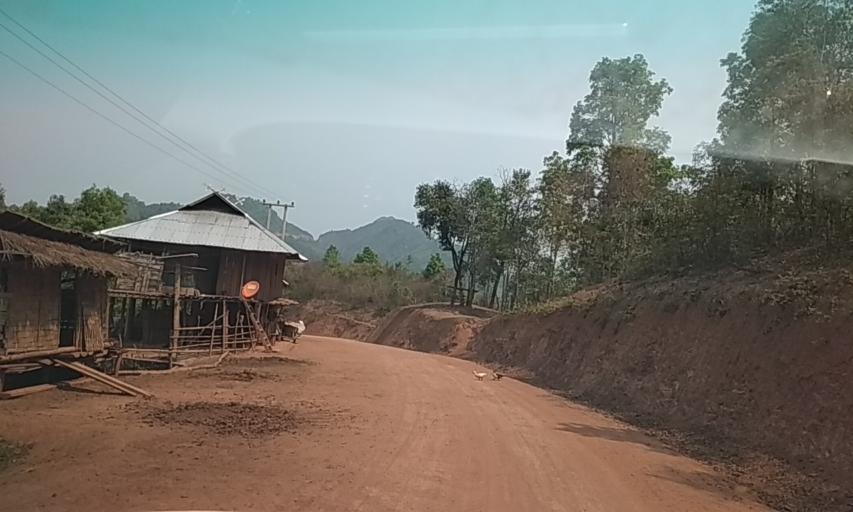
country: VN
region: Huyen Dien Bien
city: Dien Bien Phu
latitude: 21.4626
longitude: 102.7719
